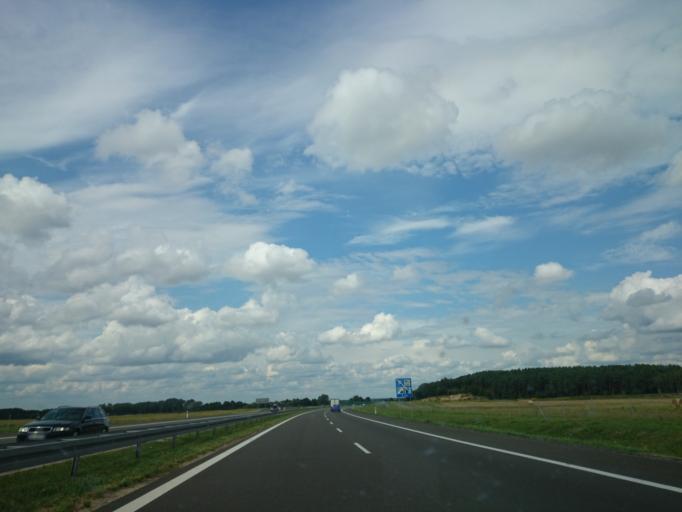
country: PL
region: Lubusz
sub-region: Powiat zielonogorski
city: Sulechow
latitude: 52.0854
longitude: 15.5840
